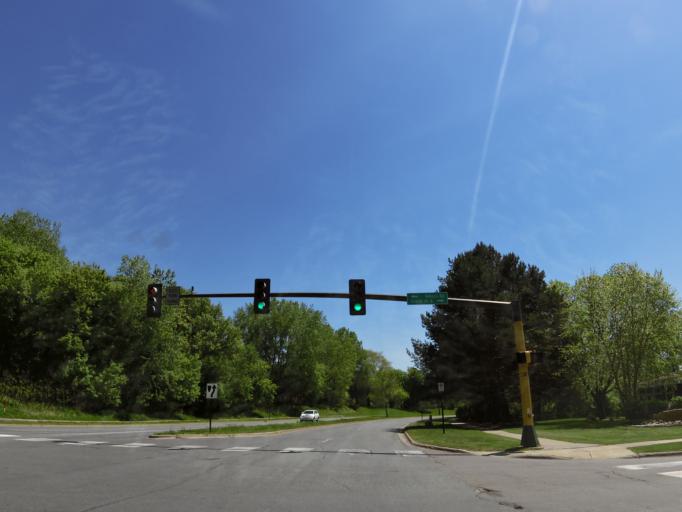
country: US
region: Minnesota
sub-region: Hennepin County
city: Edina
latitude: 44.8350
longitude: -93.3946
